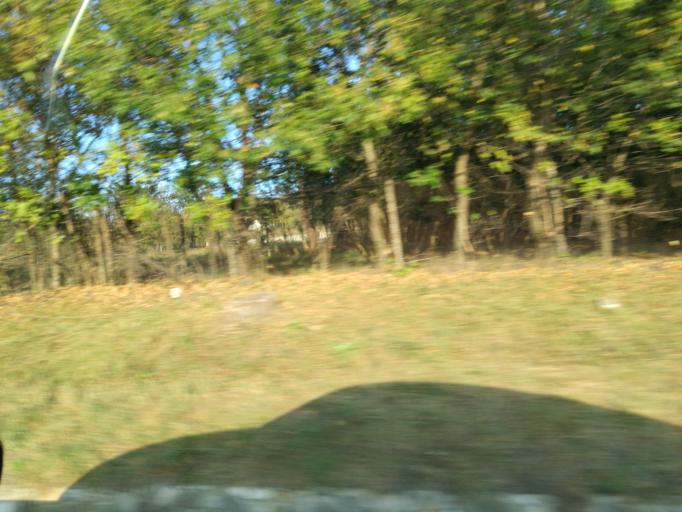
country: RO
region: Suceava
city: Bunesti-Regat
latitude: 47.5065
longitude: 26.2847
